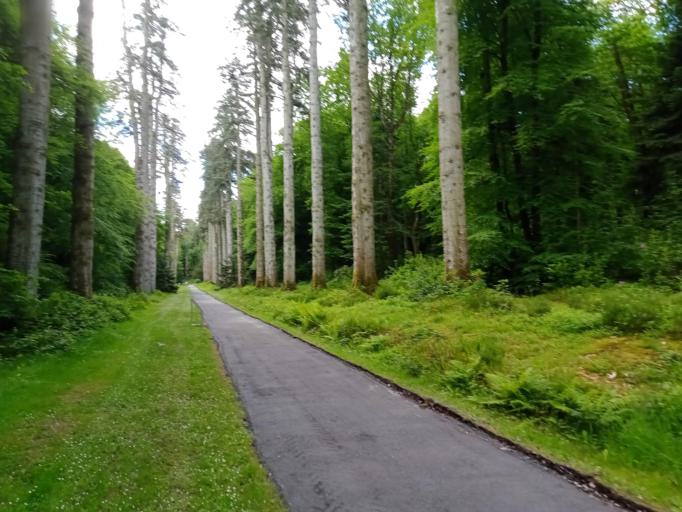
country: IE
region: Leinster
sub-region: Kilkenny
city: Thomastown
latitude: 52.4732
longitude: -7.0581
